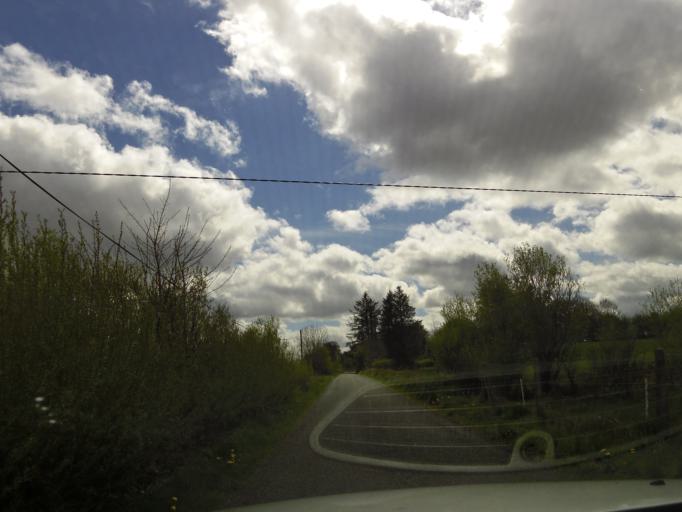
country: IE
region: Connaught
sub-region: Maigh Eo
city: Kiltamagh
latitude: 53.8027
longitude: -8.9710
